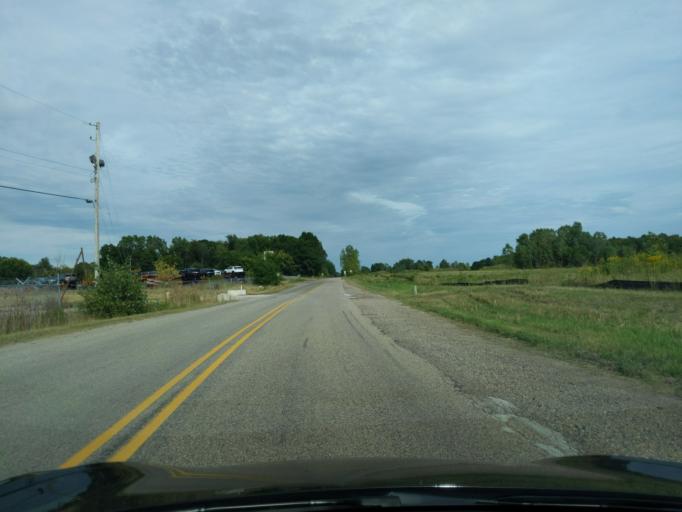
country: US
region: Michigan
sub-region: Eaton County
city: Dimondale
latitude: 42.6692
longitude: -84.6605
